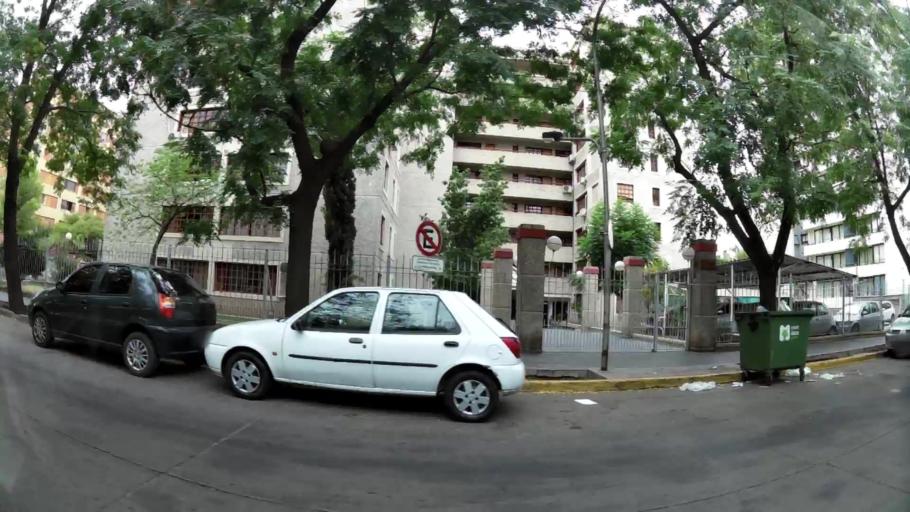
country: AR
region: Mendoza
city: Mendoza
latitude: -32.8745
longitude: -68.8444
